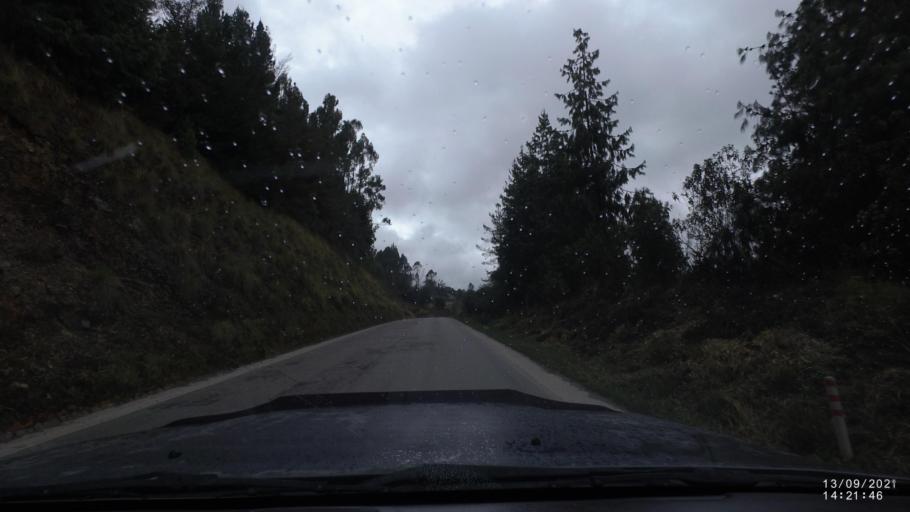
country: BO
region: Cochabamba
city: Colomi
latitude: -17.2617
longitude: -65.8874
